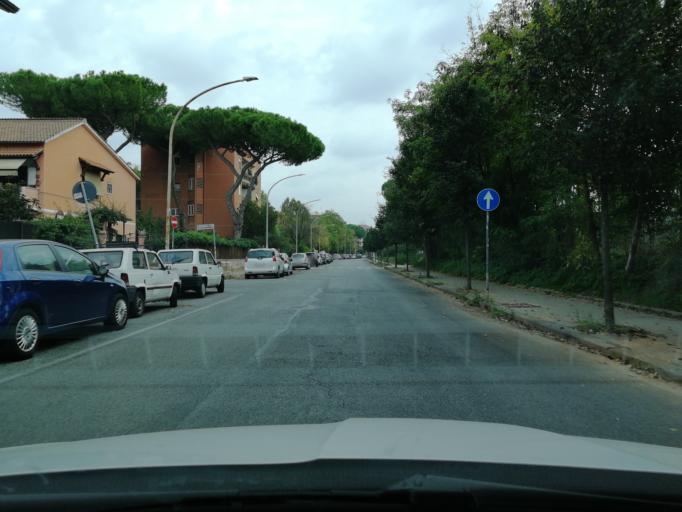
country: IT
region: Latium
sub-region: Citta metropolitana di Roma Capitale
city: Rome
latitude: 41.8557
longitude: 12.5540
